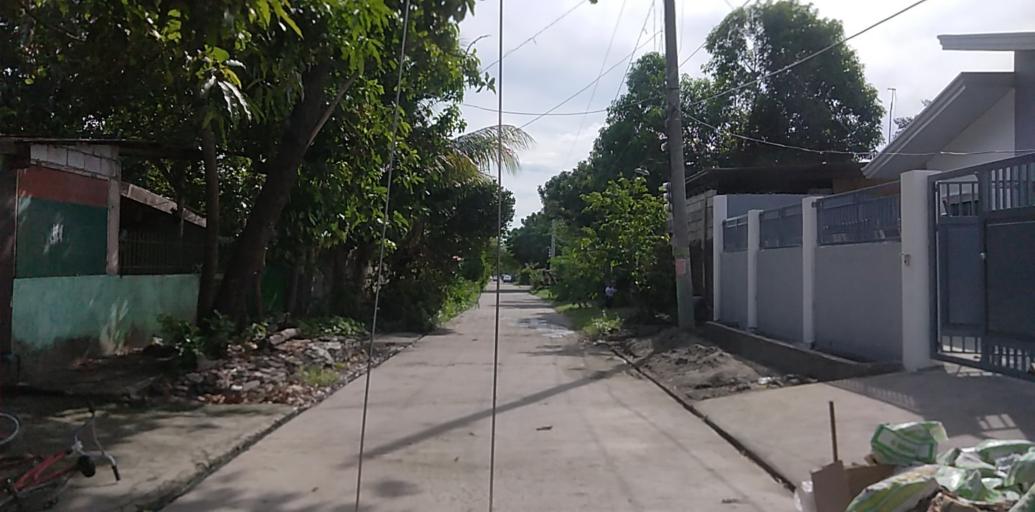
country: PH
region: Central Luzon
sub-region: Province of Pampanga
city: Angeles City
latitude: 15.1306
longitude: 120.5625
